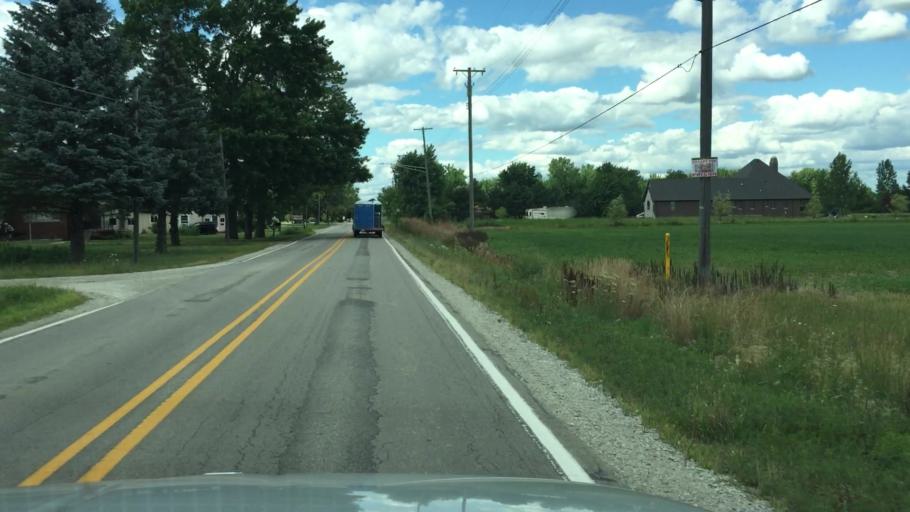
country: US
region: Michigan
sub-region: Macomb County
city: Armada
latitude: 42.9179
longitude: -82.9455
